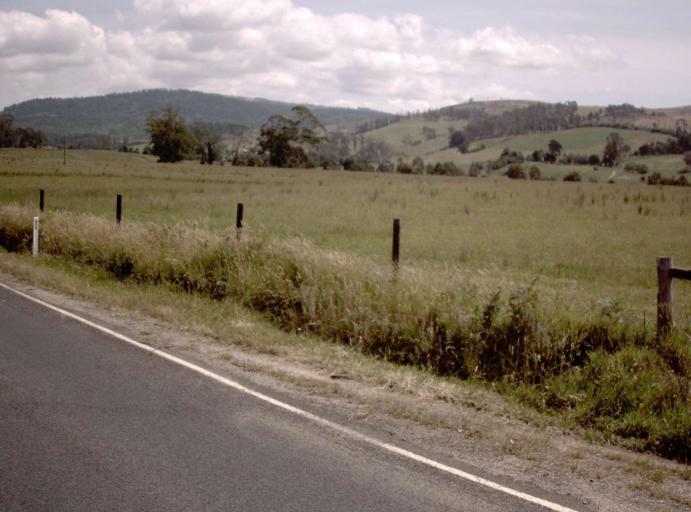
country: AU
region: Victoria
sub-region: Latrobe
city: Traralgon
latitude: -38.2972
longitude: 146.5380
